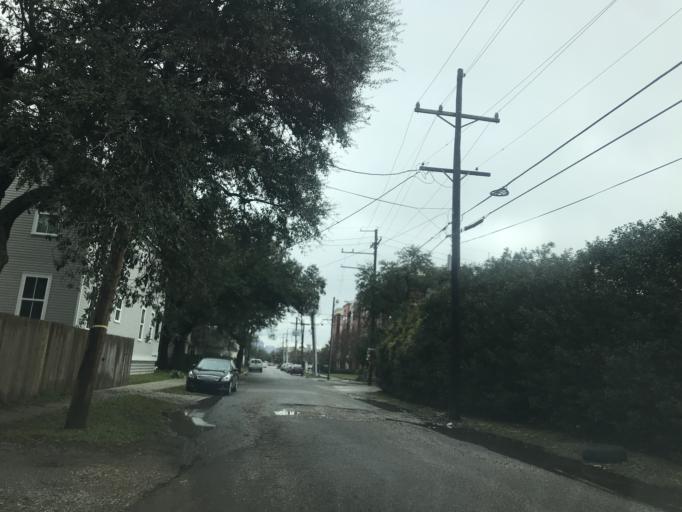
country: US
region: Louisiana
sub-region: Orleans Parish
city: New Orleans
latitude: 29.9721
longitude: -90.1092
